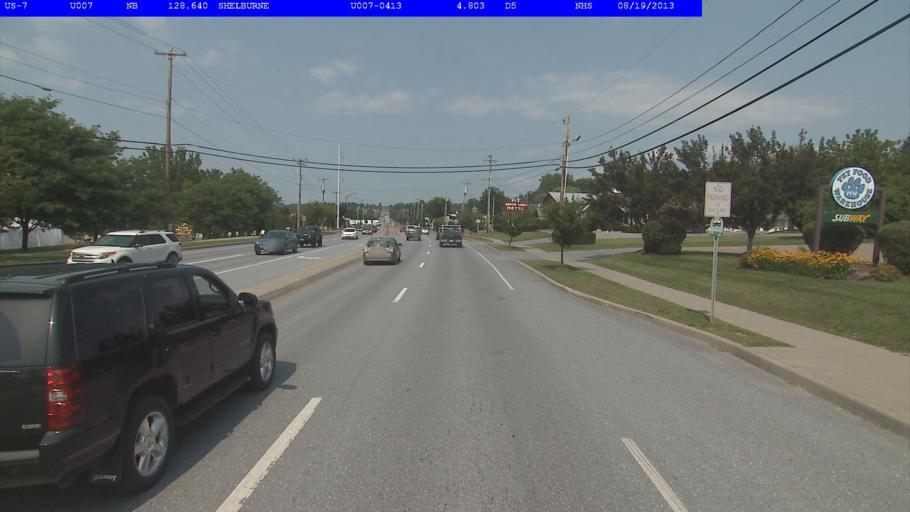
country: US
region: Vermont
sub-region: Chittenden County
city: Burlington
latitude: 44.4193
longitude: -73.2123
